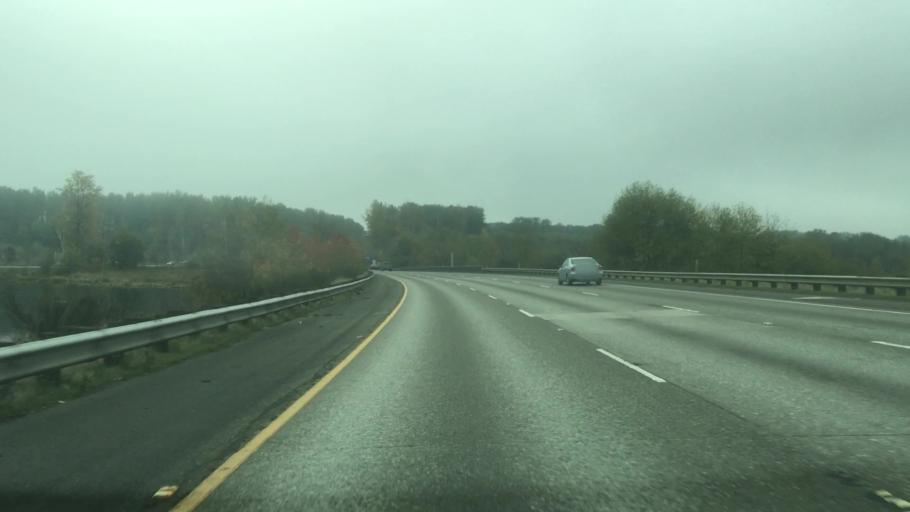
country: US
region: Washington
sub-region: Pierce County
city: DuPont
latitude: 47.0769
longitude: -122.6942
